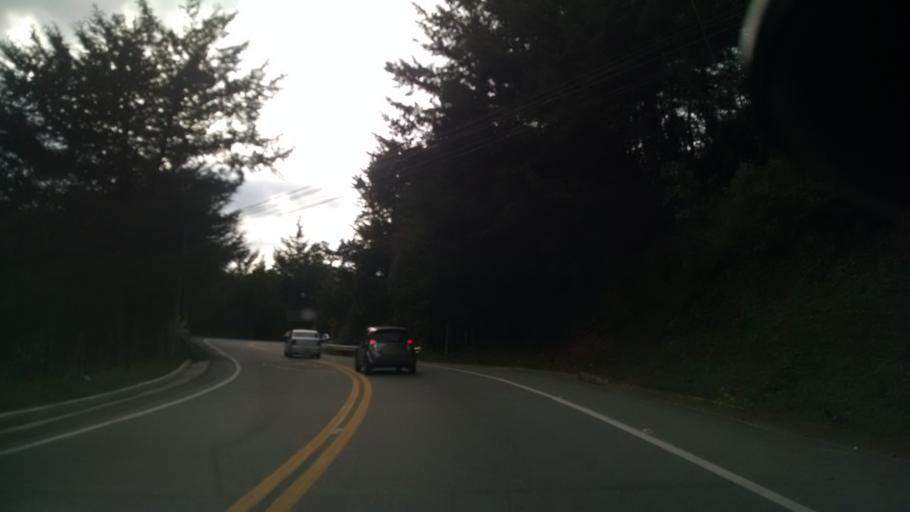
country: CO
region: Antioquia
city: El Retiro
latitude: 6.1338
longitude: -75.5075
